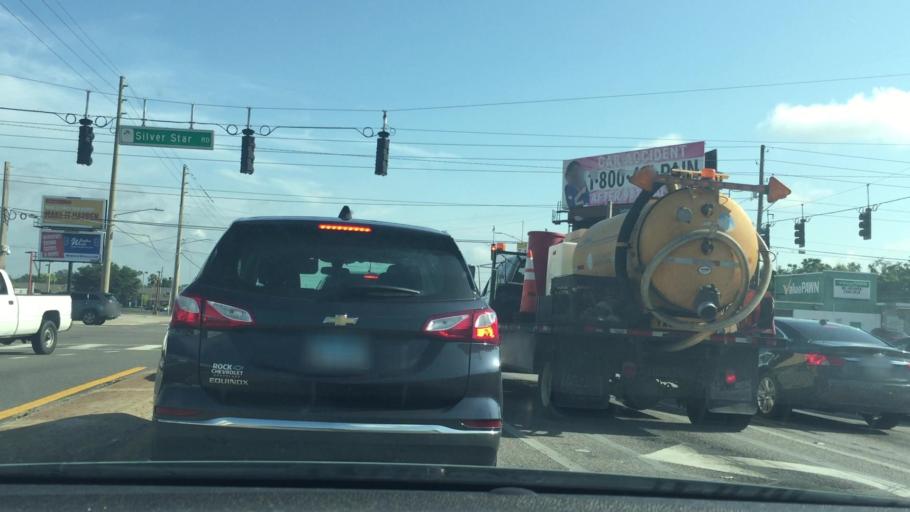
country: US
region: Florida
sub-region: Orange County
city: Pine Hills
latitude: 28.5774
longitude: -81.4518
